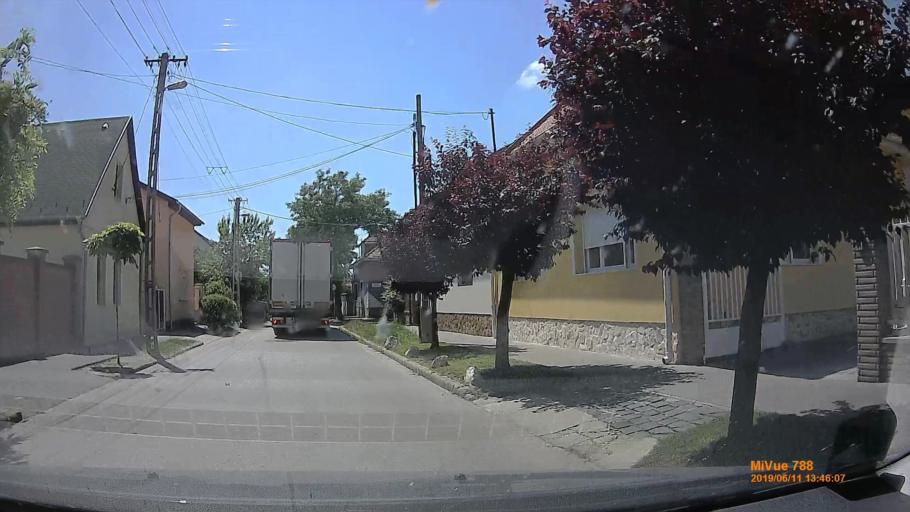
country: HU
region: Budapest
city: Budapest XXIII. keruelet
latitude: 47.3887
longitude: 19.1163
